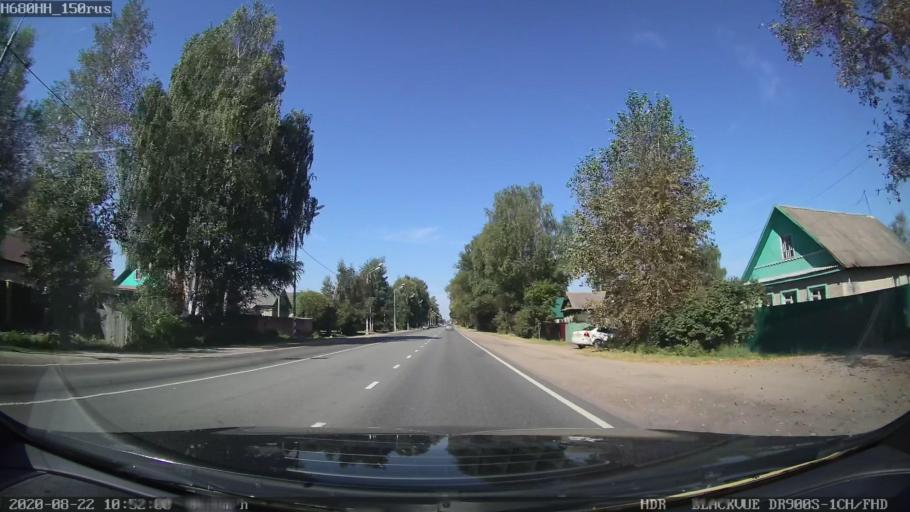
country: RU
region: Tverskaya
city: Emmaus
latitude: 56.7920
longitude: 36.0678
